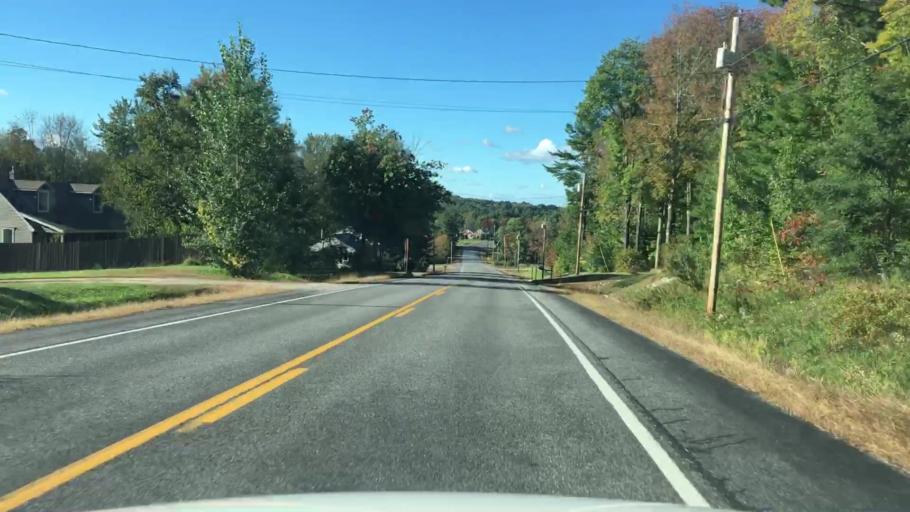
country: US
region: Maine
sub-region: Androscoggin County
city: Lisbon
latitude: 44.0381
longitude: -70.0734
